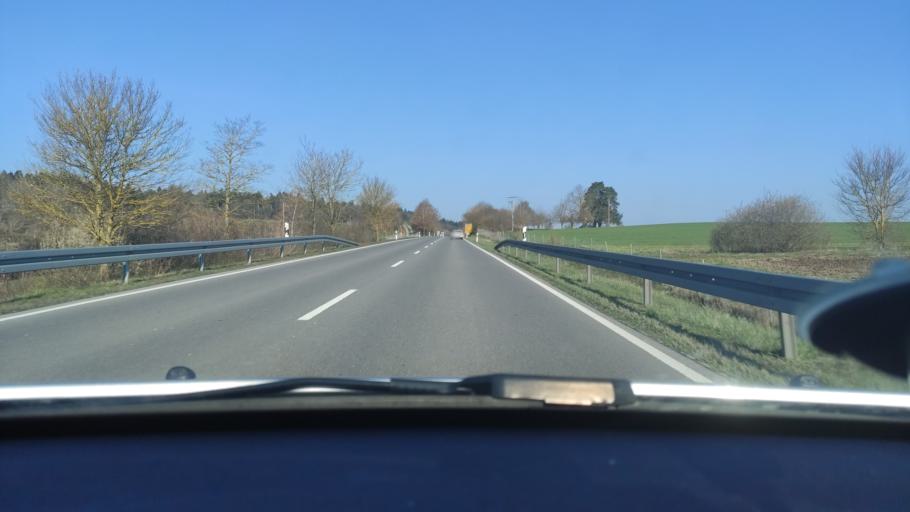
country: DE
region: Baden-Wuerttemberg
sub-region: Tuebingen Region
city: Haigerloch
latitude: 48.3607
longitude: 8.7733
